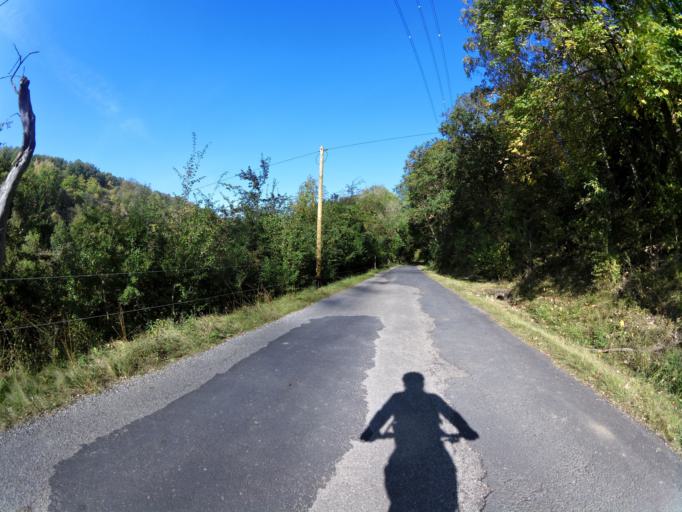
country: DE
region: Bavaria
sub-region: Regierungsbezirk Unterfranken
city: Ochsenfurt
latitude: 49.6783
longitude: 10.0464
